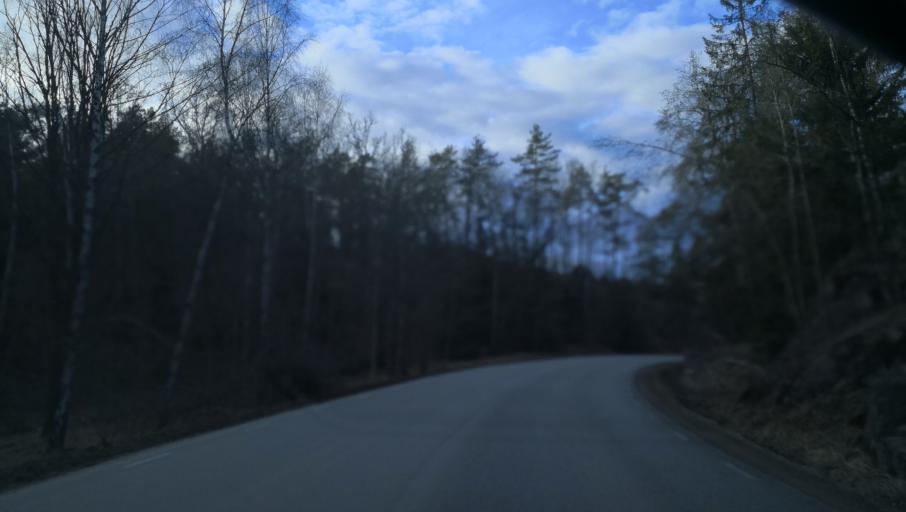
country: SE
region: Stockholm
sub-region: Varmdo Kommun
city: Gustavsberg
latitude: 59.3431
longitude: 18.3559
